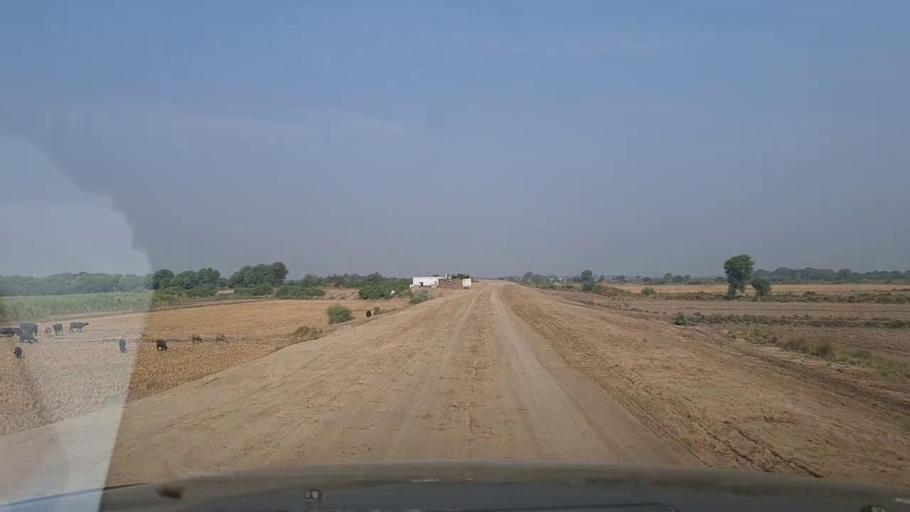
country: PK
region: Sindh
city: Bulri
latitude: 25.0016
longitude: 68.2886
